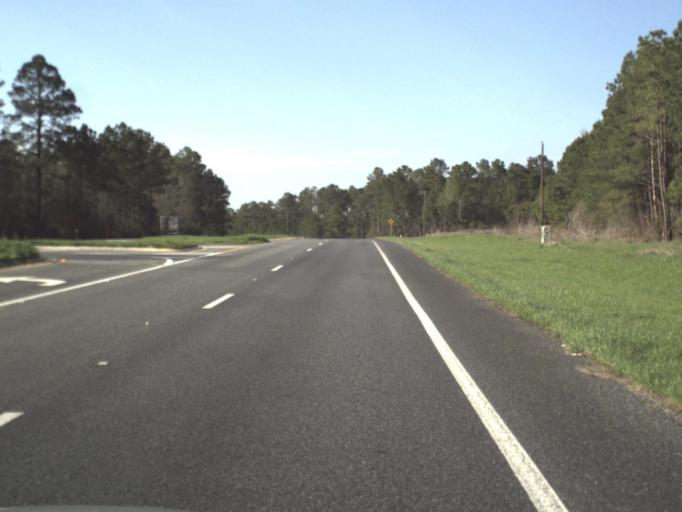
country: US
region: Florida
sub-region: Jefferson County
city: Monticello
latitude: 30.6618
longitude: -83.8783
